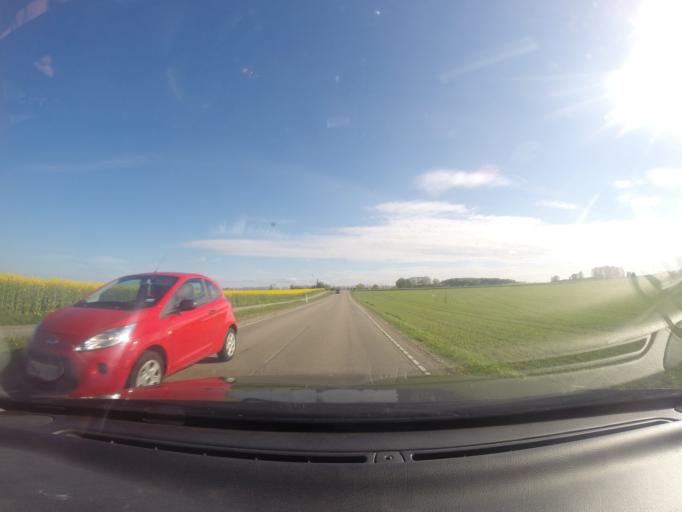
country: DK
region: Capital Region
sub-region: Hoje-Taastrup Kommune
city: Taastrup
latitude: 55.6736
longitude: 12.2539
